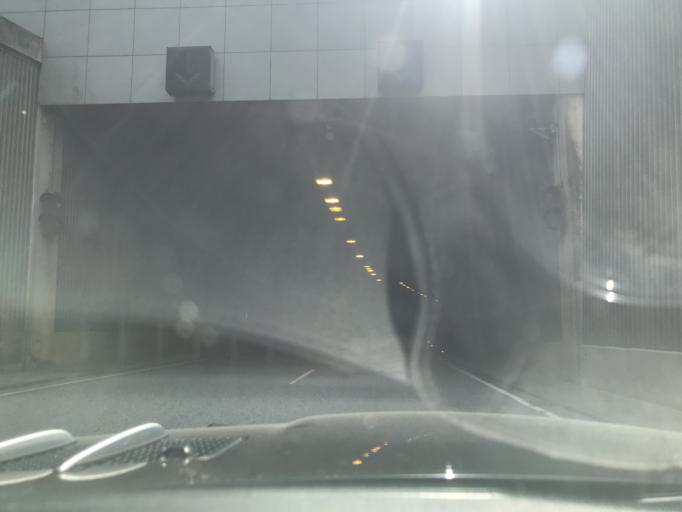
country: DE
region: Schleswig-Holstein
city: Ratekau
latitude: 53.9037
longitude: 10.7788
